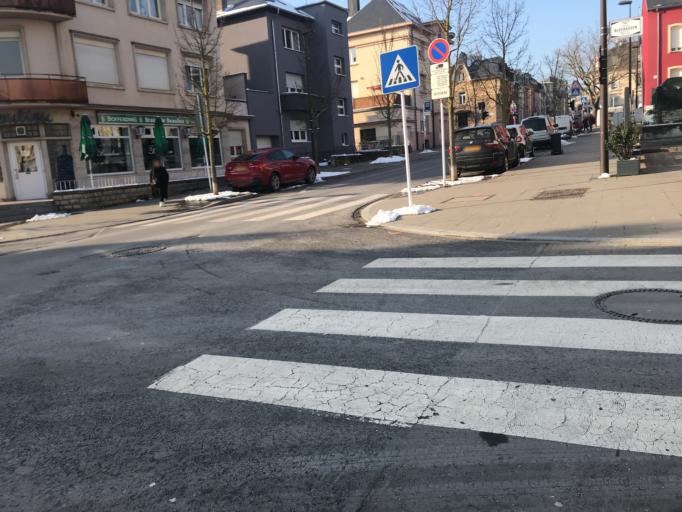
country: LU
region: Luxembourg
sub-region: Canton de Luxembourg
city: Luxembourg
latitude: 49.6013
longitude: 6.1399
